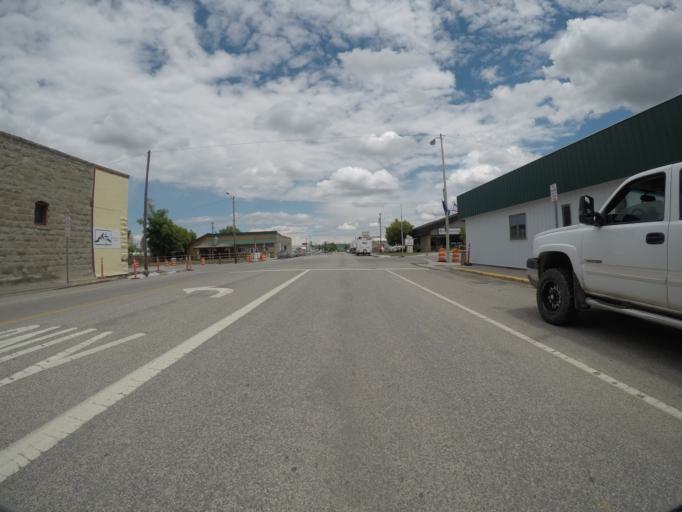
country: US
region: Montana
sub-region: Sweet Grass County
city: Big Timber
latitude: 45.8349
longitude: -109.9561
